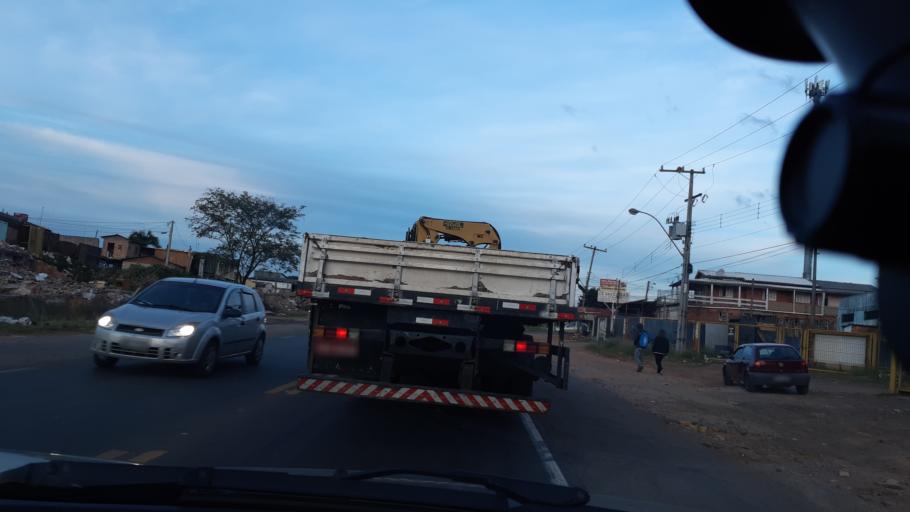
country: BR
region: Rio Grande do Sul
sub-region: Sapucaia Do Sul
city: Sapucaia
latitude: -29.8368
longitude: -51.1566
